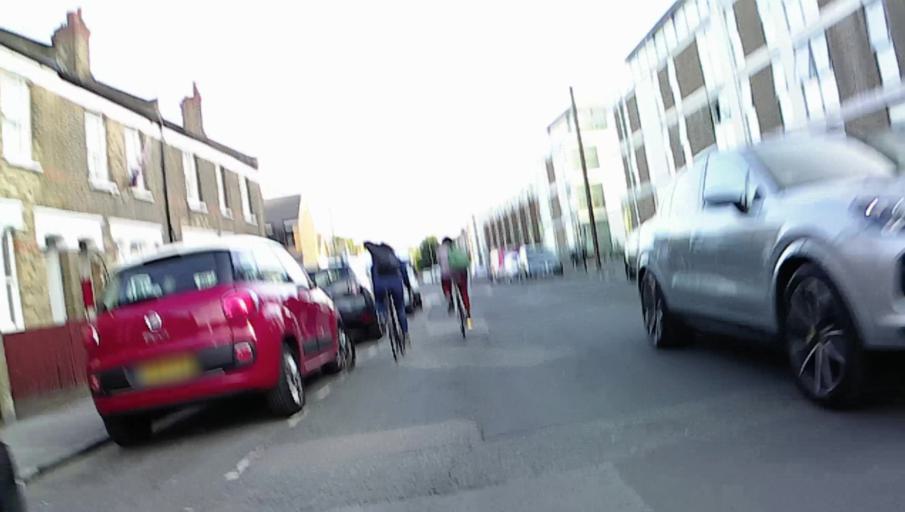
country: GB
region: England
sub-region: Greater London
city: Blackheath
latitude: 51.4886
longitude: 0.0045
